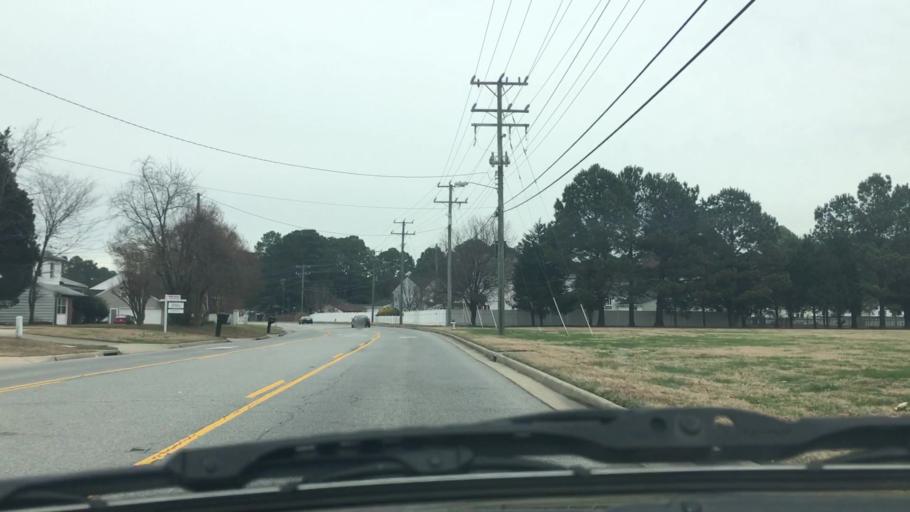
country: US
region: Virginia
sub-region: City of Portsmouth
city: Portsmouth Heights
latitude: 36.8594
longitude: -76.3771
